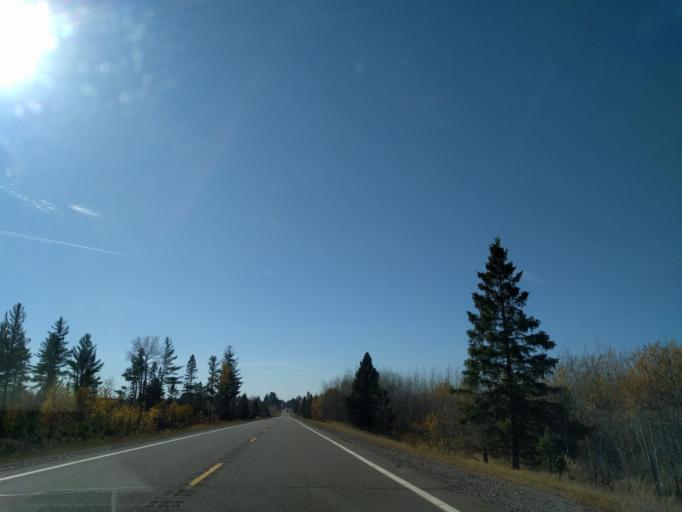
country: US
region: Michigan
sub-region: Marquette County
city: West Ishpeming
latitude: 46.4555
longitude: -87.9436
